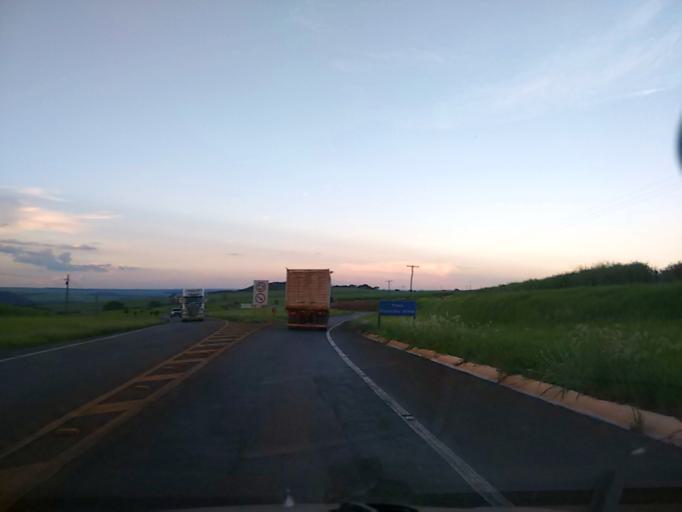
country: BR
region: Sao Paulo
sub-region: Boa Esperanca Do Sul
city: Boa Esperanca do Sul
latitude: -22.1220
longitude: -48.4570
